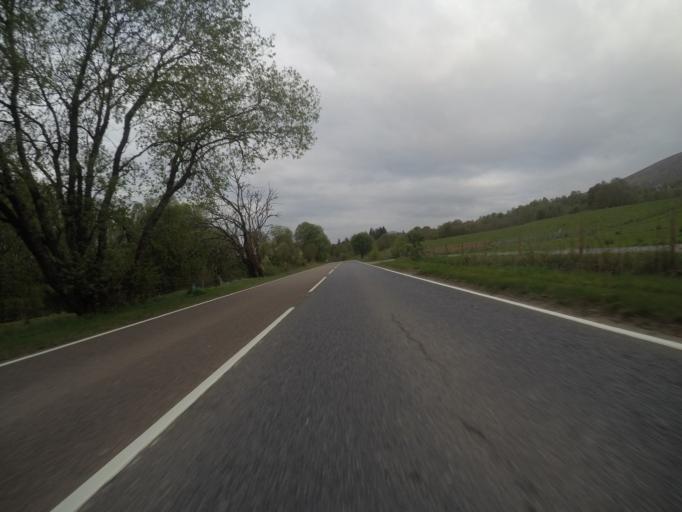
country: GB
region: Scotland
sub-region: Highland
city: Spean Bridge
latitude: 56.8907
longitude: -4.8700
